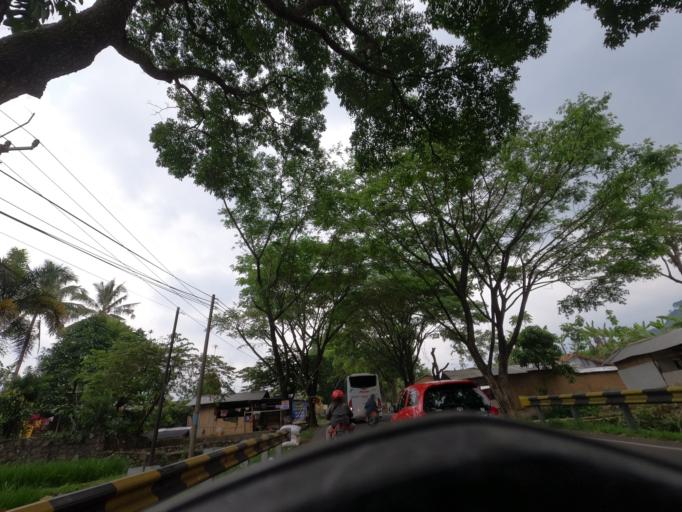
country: ID
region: West Java
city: Ciranjang-hilir
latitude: -6.7923
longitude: 107.0725
